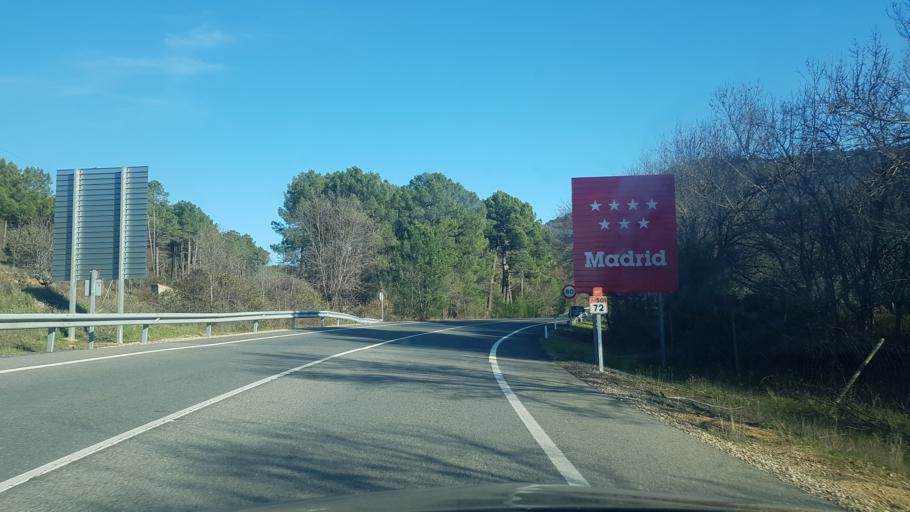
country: ES
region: Castille and Leon
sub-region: Provincia de Avila
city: Casillas
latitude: 40.3053
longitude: -4.5348
